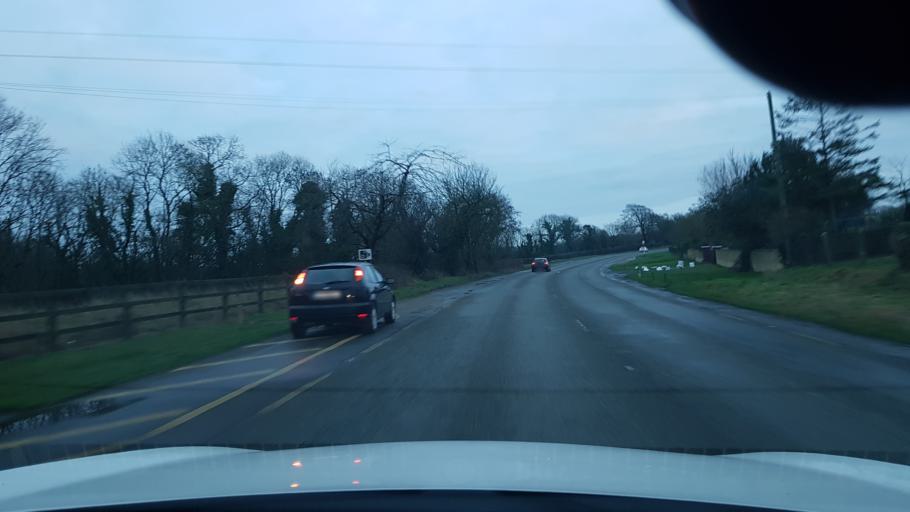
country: IE
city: Kentstown
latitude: 53.5898
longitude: -6.5975
